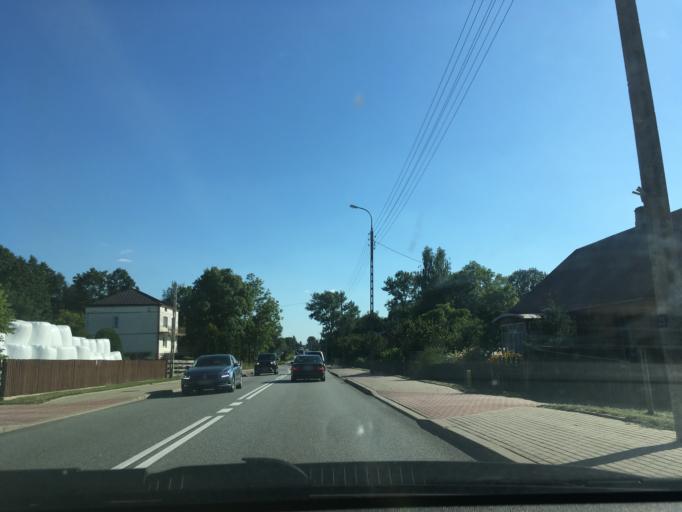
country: PL
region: Podlasie
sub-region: Powiat sokolski
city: Suchowola
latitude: 53.5077
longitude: 23.0990
